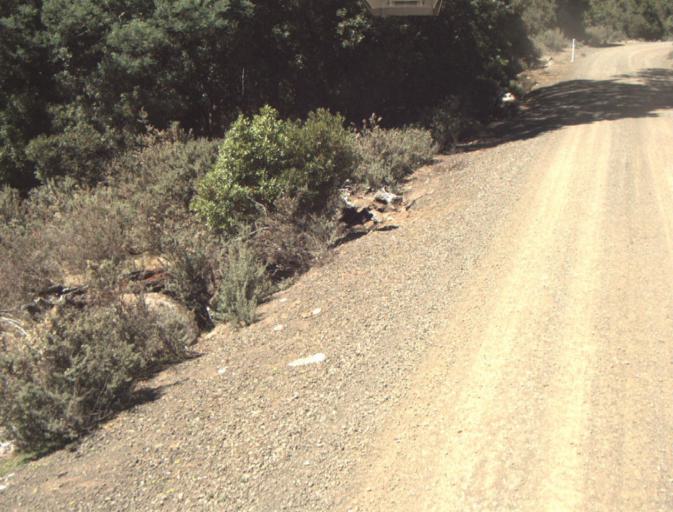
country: AU
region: Tasmania
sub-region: Dorset
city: Scottsdale
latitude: -41.3638
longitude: 147.4314
